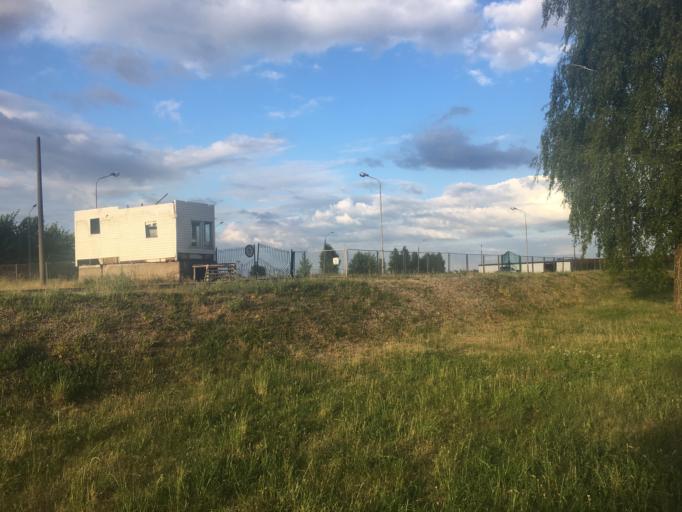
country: BY
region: Grodnenskaya
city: Hrodna
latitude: 53.6843
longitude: 23.8042
